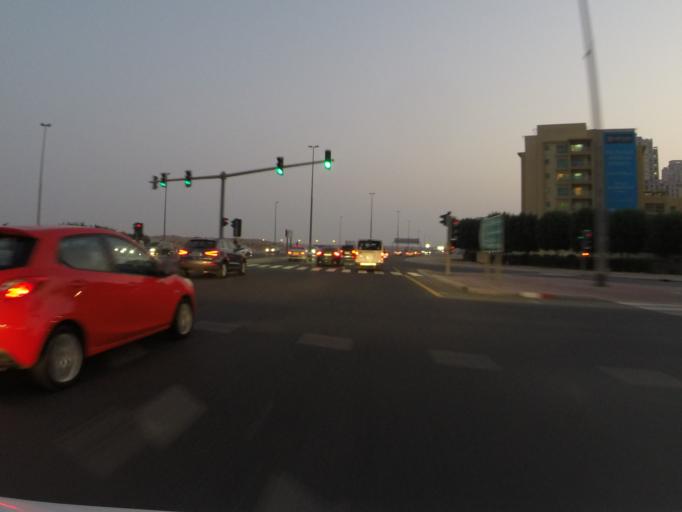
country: AE
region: Dubai
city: Dubai
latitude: 25.0914
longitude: 55.1763
